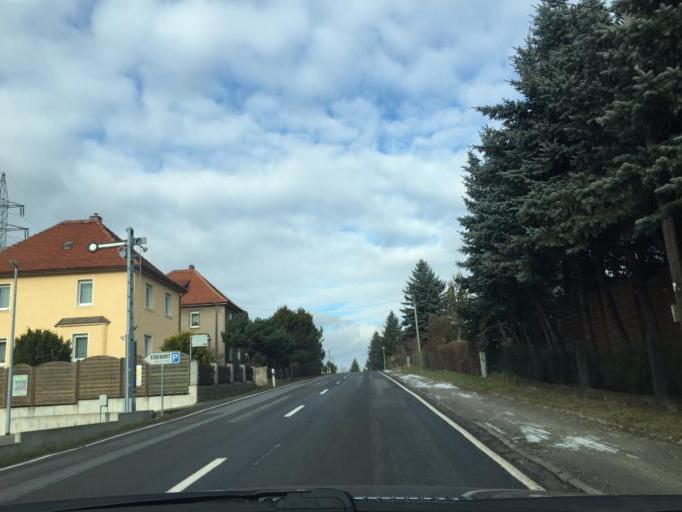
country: DE
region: Saxony
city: Radeberg
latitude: 51.1372
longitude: 13.9163
